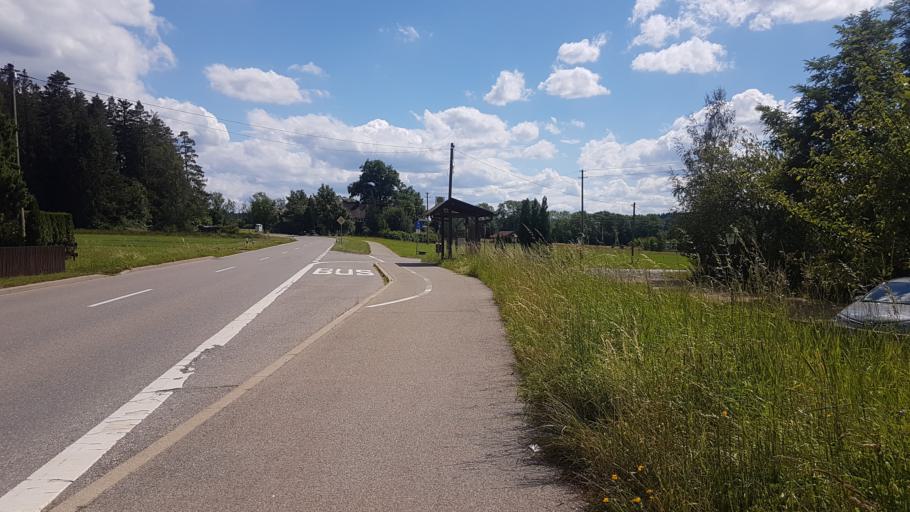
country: DE
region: Baden-Wuerttemberg
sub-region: Freiburg Region
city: Hardt
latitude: 48.2087
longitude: 8.4127
